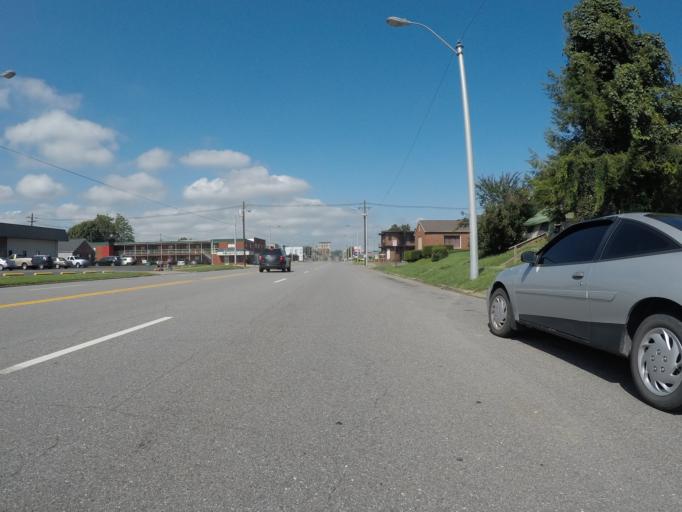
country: US
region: Kentucky
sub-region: Boyd County
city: Ashland
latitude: 38.4738
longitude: -82.6298
